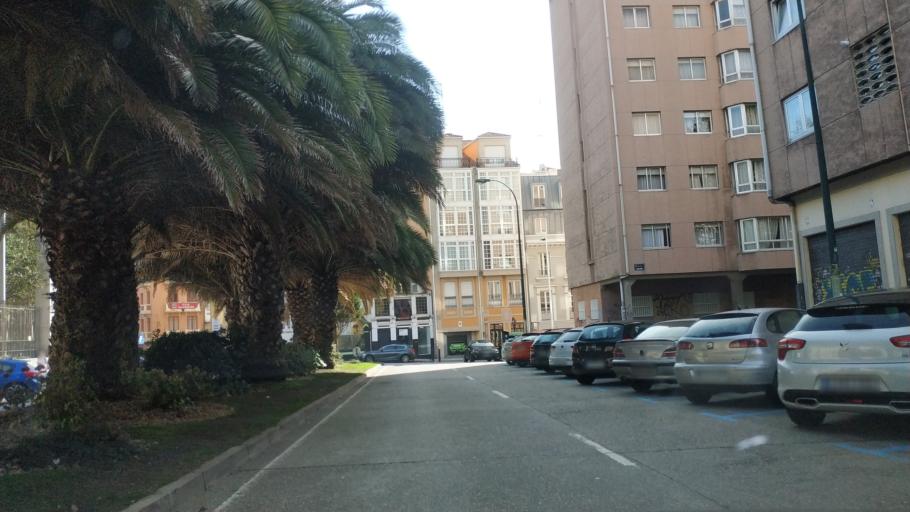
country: ES
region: Galicia
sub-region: Provincia da Coruna
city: A Coruna
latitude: 43.3728
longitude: -8.4004
